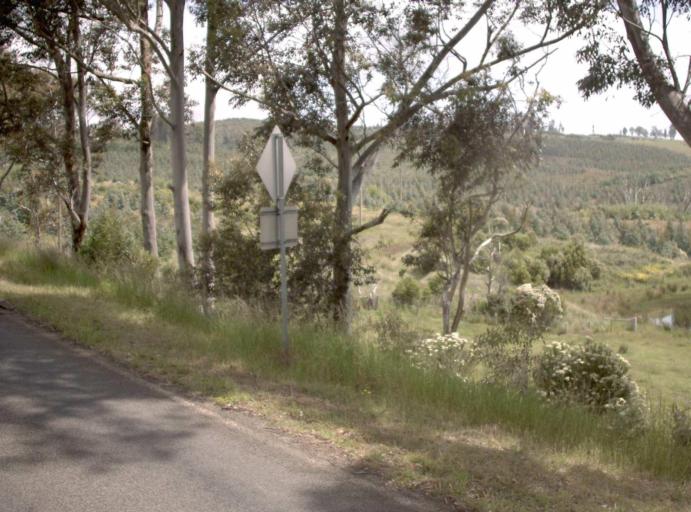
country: AU
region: Victoria
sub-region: Latrobe
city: Traralgon
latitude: -38.3527
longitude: 146.5683
